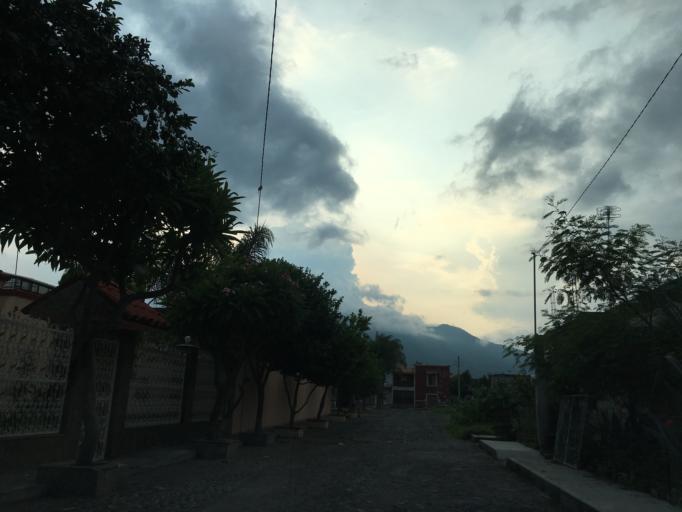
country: MX
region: Nayarit
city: Jala
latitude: 21.0981
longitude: -104.4337
